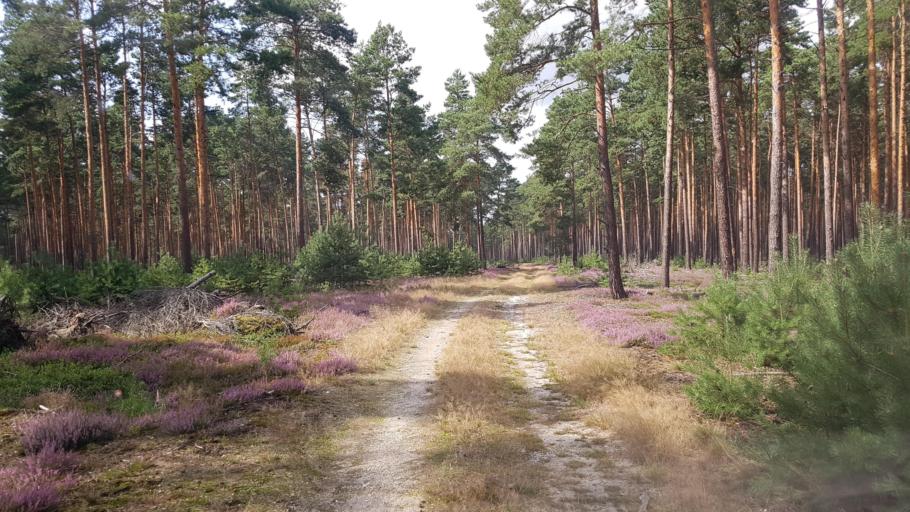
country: DE
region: Brandenburg
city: Schonborn
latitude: 51.6511
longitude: 13.4831
